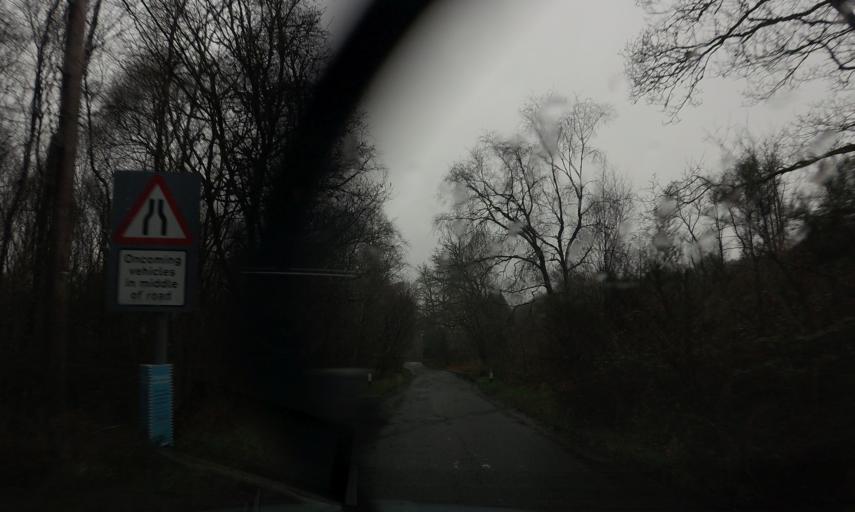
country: GB
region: Scotland
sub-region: West Dunbartonshire
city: Balloch
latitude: 56.1323
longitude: -4.6110
